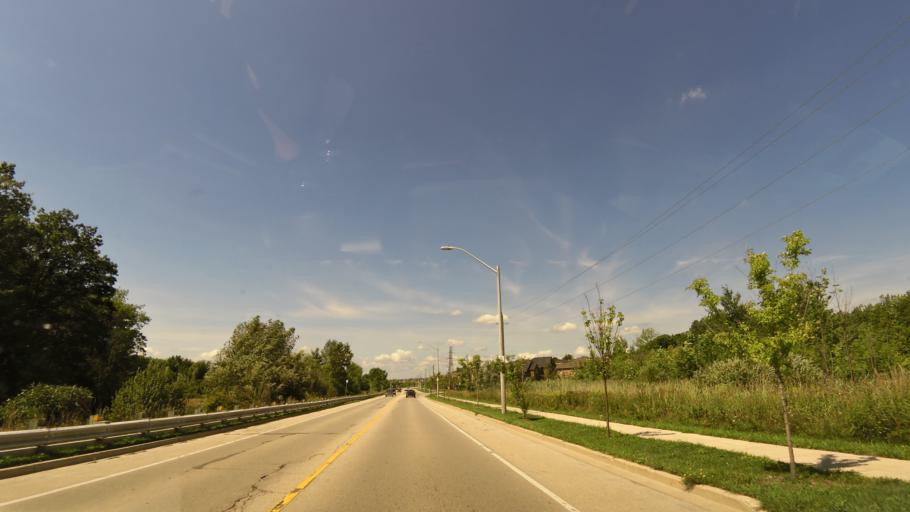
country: CA
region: Ontario
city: Ancaster
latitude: 43.2218
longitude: -79.9310
